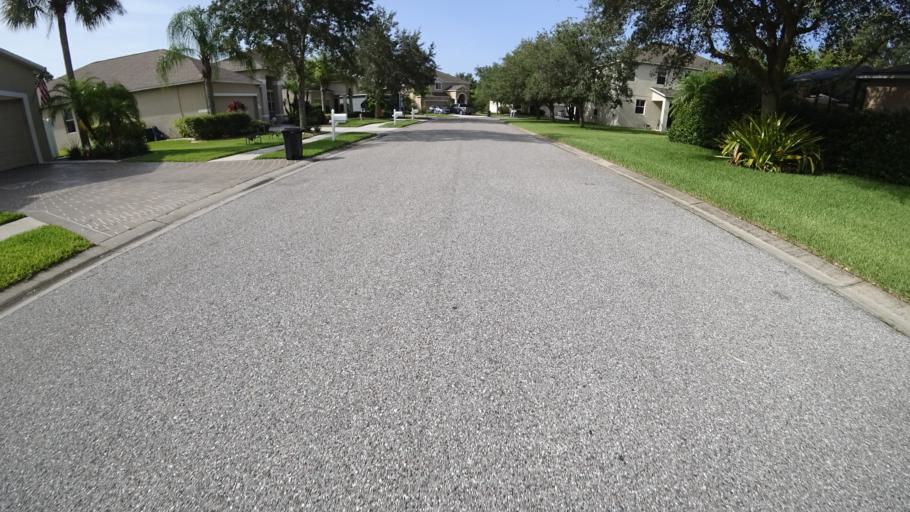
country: US
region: Florida
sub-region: Manatee County
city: Ellenton
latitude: 27.5572
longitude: -82.4957
